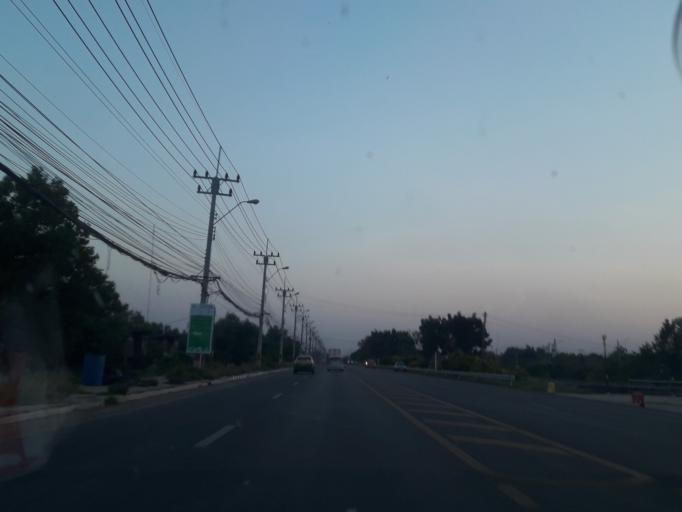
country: TH
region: Pathum Thani
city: Thanyaburi
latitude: 14.0781
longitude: 100.7102
